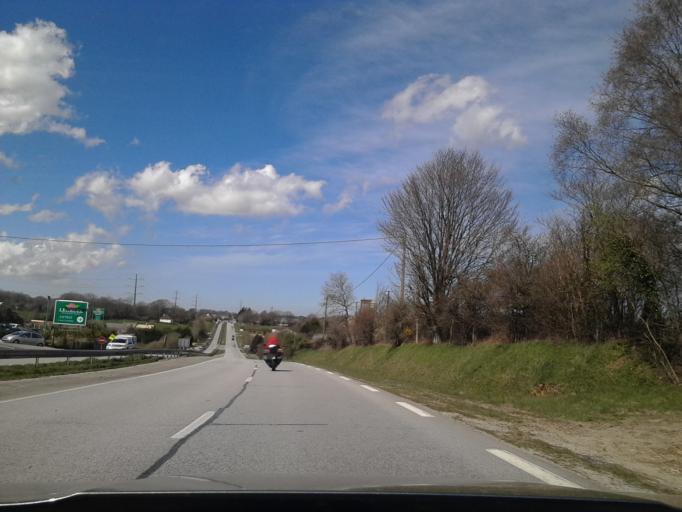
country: FR
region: Lower Normandy
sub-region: Departement de la Manche
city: La Glacerie
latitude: 49.5770
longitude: -1.5807
